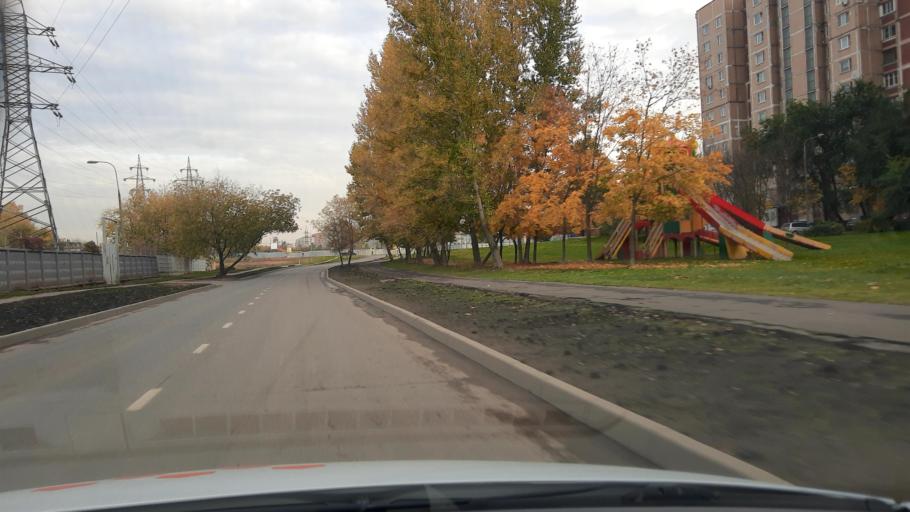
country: RU
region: Moskovskaya
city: Kur'yanovo
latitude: 55.6602
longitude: 37.7064
